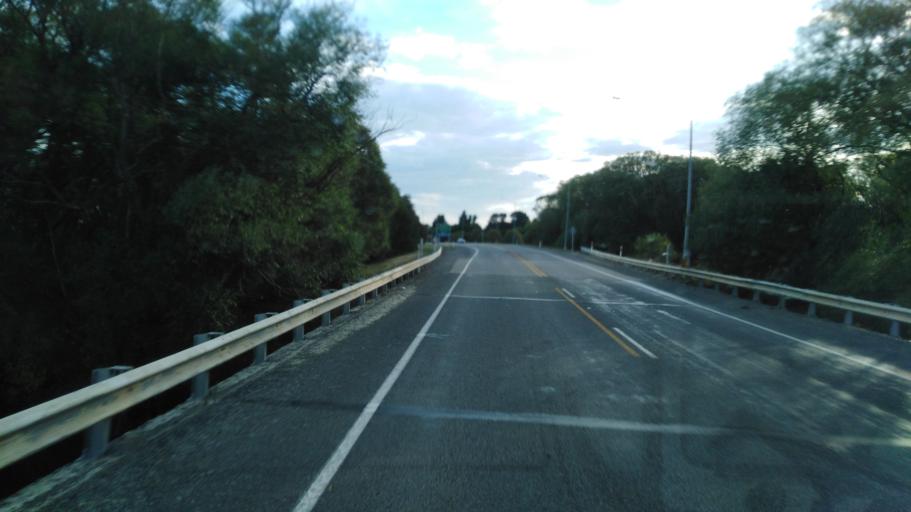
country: NZ
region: Canterbury
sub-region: Waimakariri District
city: Kaiapoi
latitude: -43.3553
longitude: 172.6596
